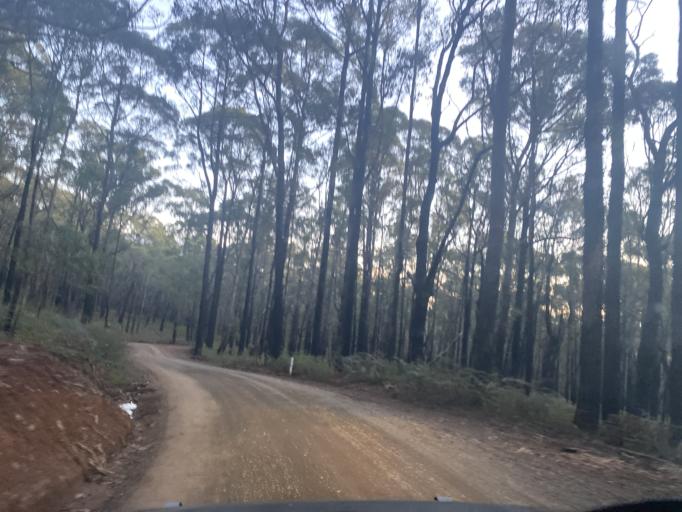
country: AU
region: Victoria
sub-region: Yarra Ranges
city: Healesville
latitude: -37.4415
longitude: 145.4990
